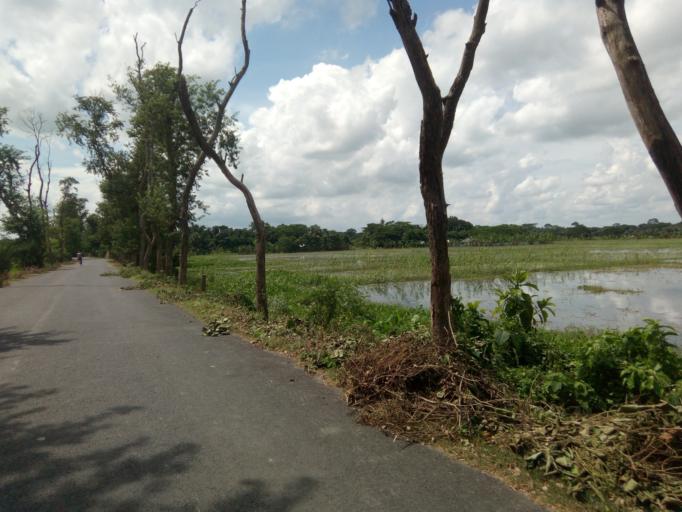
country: BD
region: Khulna
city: Kalia
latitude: 23.0142
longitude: 89.7238
